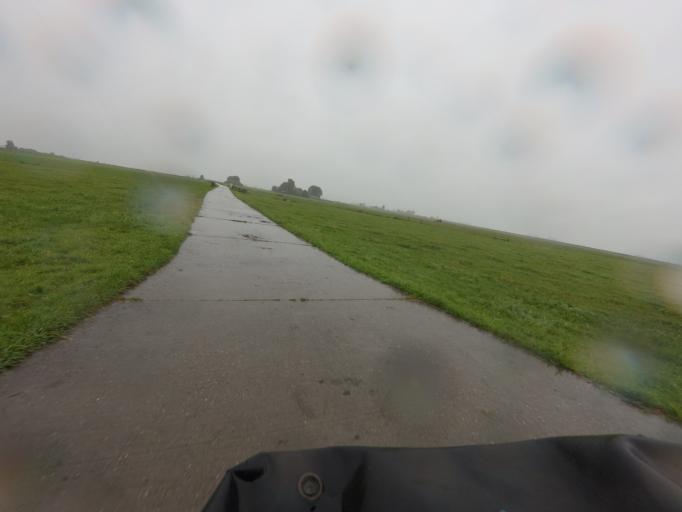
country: NL
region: Friesland
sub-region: Sudwest Fryslan
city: Bolsward
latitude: 53.0046
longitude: 5.5210
